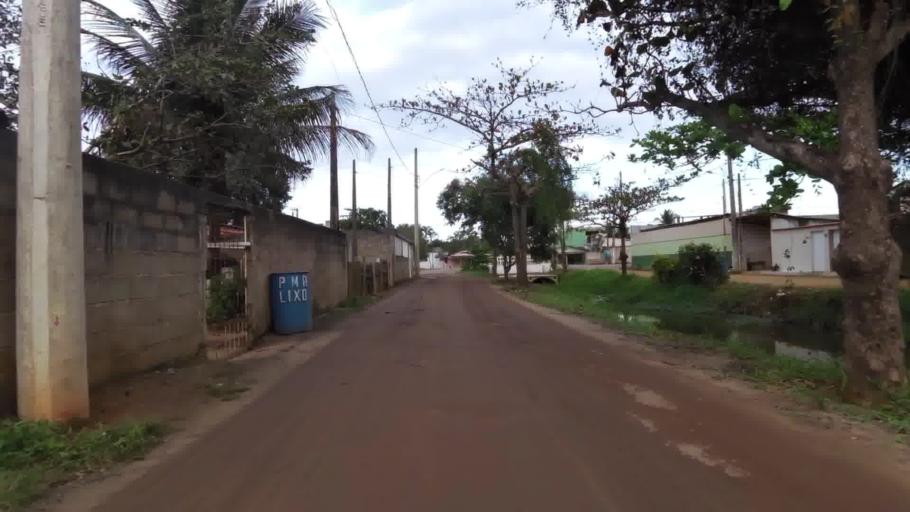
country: BR
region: Espirito Santo
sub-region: Piuma
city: Piuma
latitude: -20.8071
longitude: -40.6373
